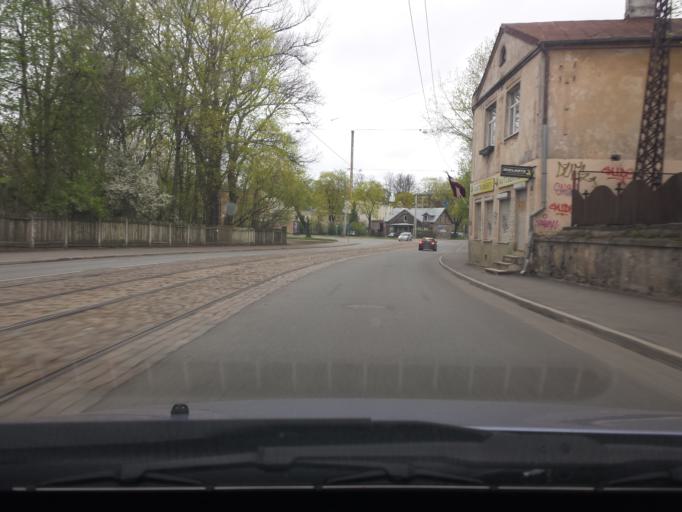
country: LV
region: Riga
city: Riga
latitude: 56.9510
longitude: 24.0645
